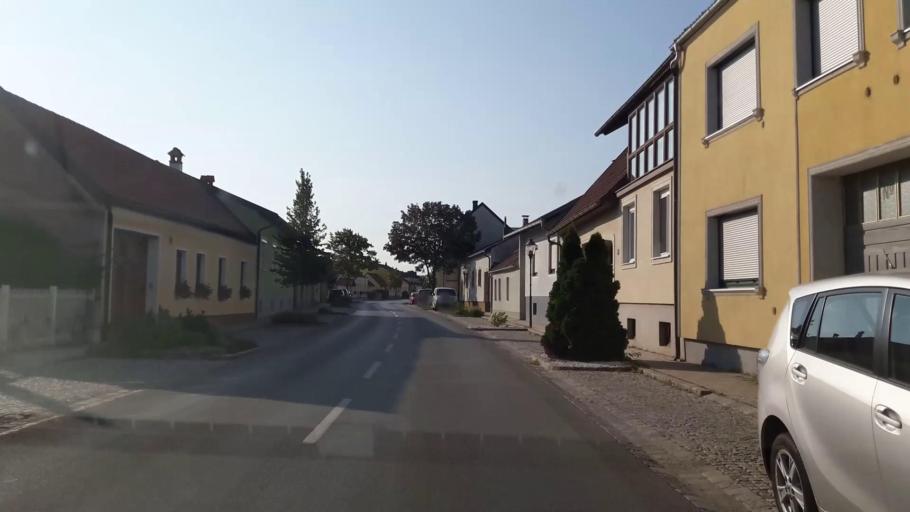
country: AT
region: Lower Austria
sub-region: Politischer Bezirk Bruck an der Leitha
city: Bruck an der Leitha
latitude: 48.0450
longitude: 16.7439
